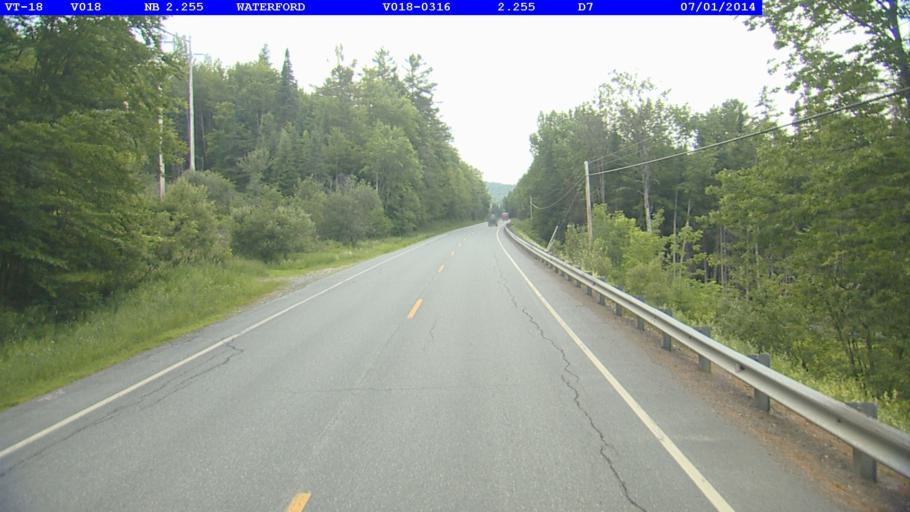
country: US
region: Vermont
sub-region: Caledonia County
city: Saint Johnsbury
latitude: 44.3689
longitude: -71.9074
